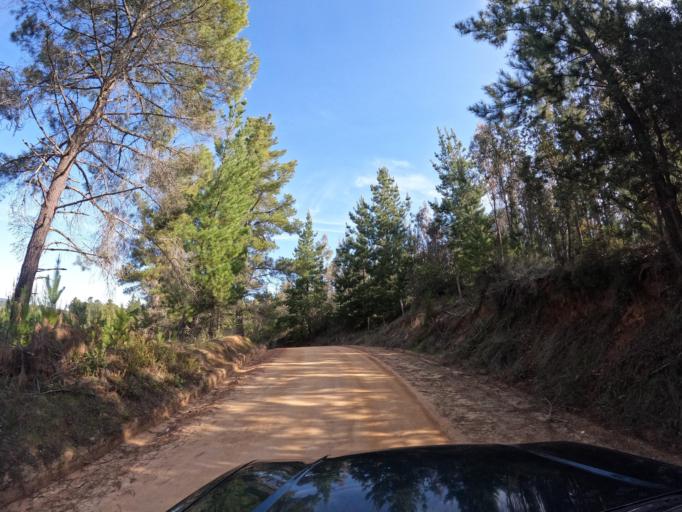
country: CL
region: Biobio
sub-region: Provincia de Biobio
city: La Laja
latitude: -37.1186
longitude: -72.7380
